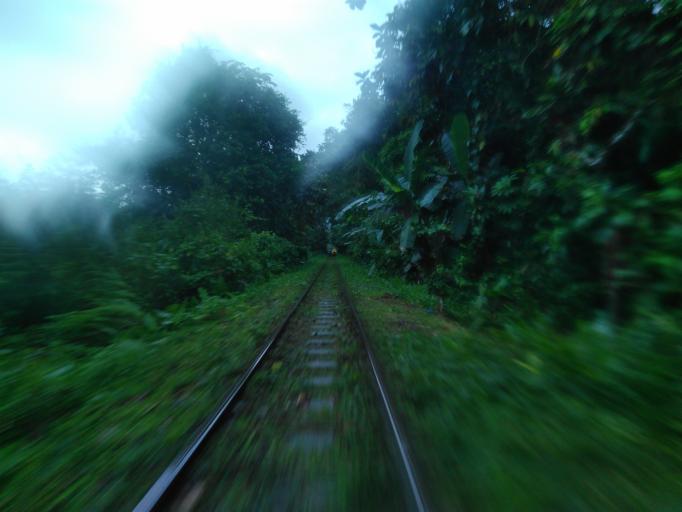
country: CO
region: Valle del Cauca
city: Buenaventura
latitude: 3.8472
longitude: -76.8631
